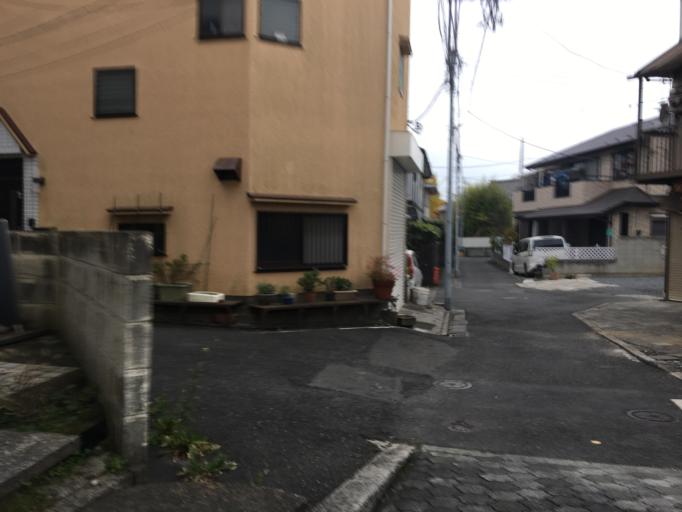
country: JP
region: Tokyo
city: Urayasu
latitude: 35.6789
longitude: 139.8852
